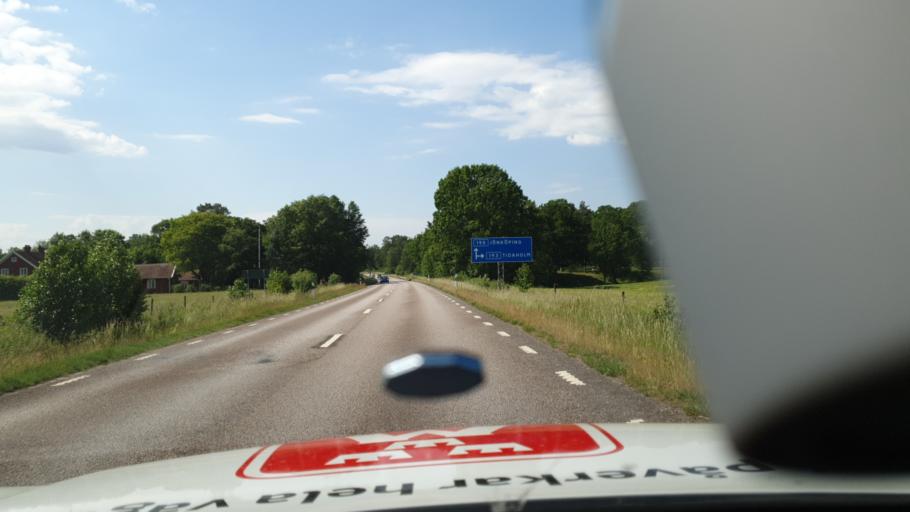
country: SE
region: Vaestra Goetaland
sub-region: Hjo Kommun
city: Hjo
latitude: 58.2292
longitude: 14.2143
